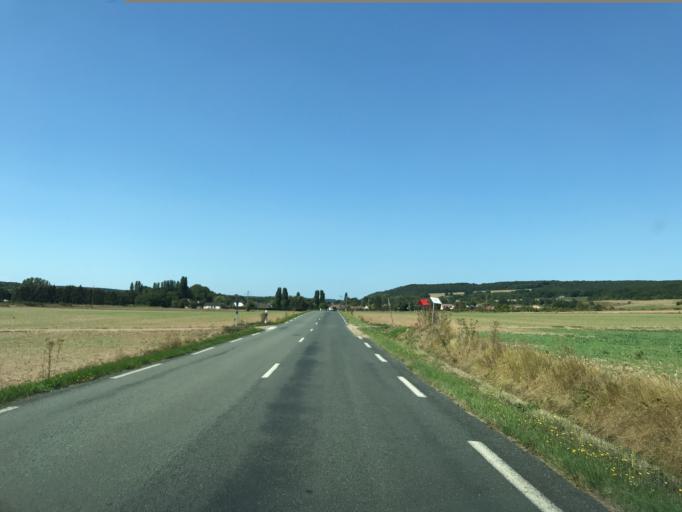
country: FR
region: Haute-Normandie
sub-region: Departement de l'Eure
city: Heudreville-sur-Eure
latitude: 49.1197
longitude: 1.2223
